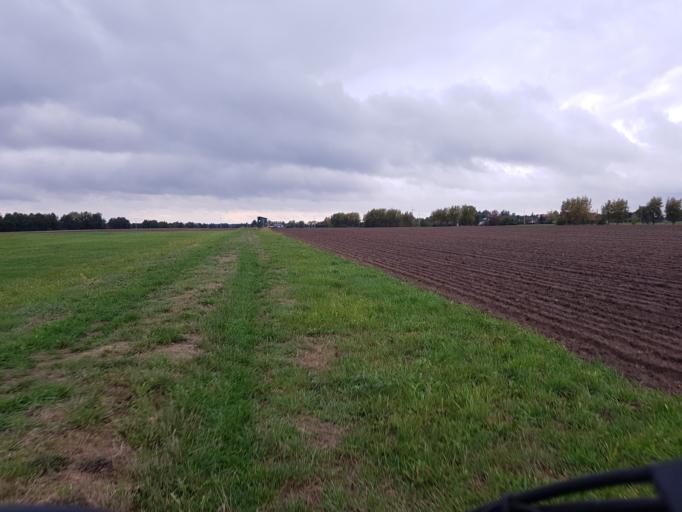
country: DE
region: Brandenburg
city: Schilda
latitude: 51.6120
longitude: 13.3672
